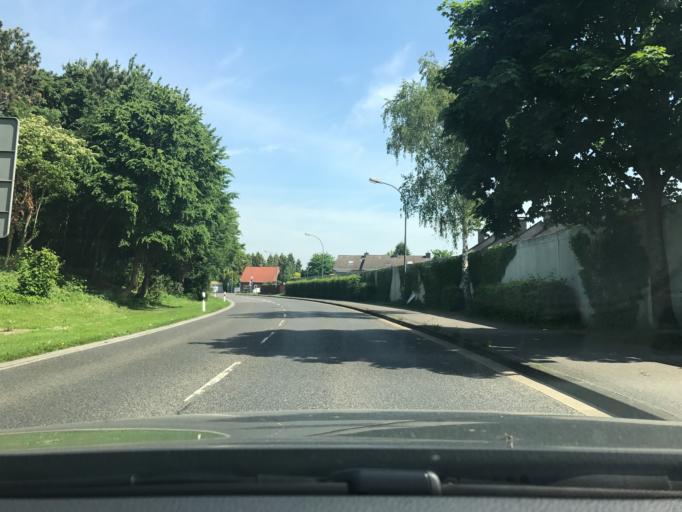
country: DE
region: North Rhine-Westphalia
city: Tonisvorst
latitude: 51.3169
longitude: 6.5049
